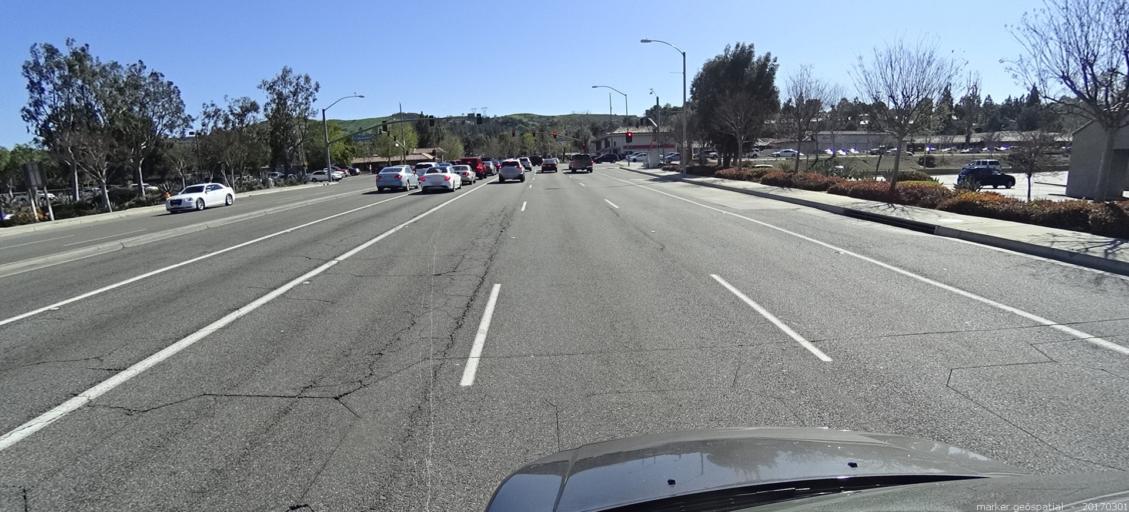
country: US
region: California
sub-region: Orange County
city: Yorba Linda
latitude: 33.8523
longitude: -117.7907
